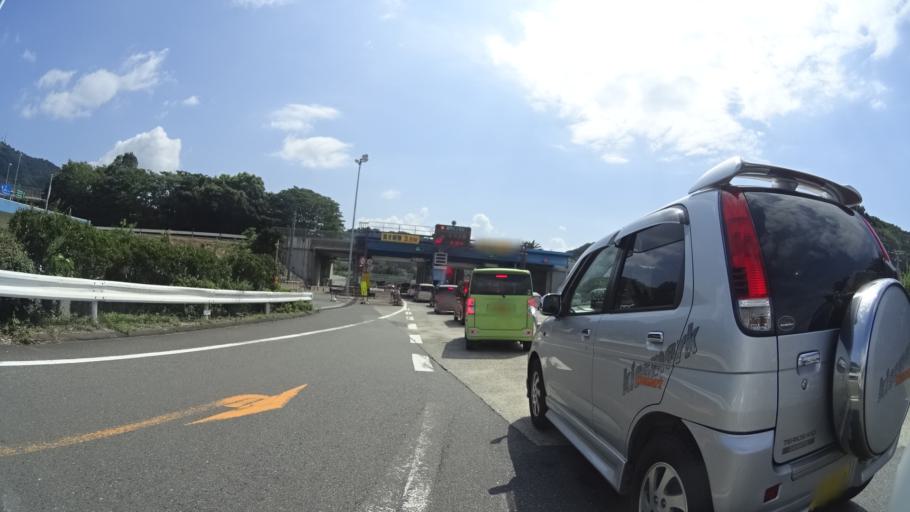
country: JP
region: Yamaguchi
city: Shimonoseki
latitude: 33.9778
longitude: 130.9465
